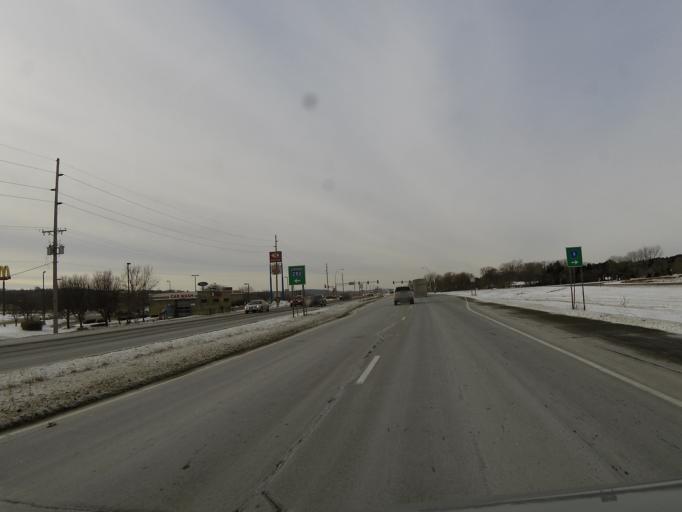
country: US
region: Minnesota
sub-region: Scott County
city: Jordan
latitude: 44.6717
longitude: -93.6371
